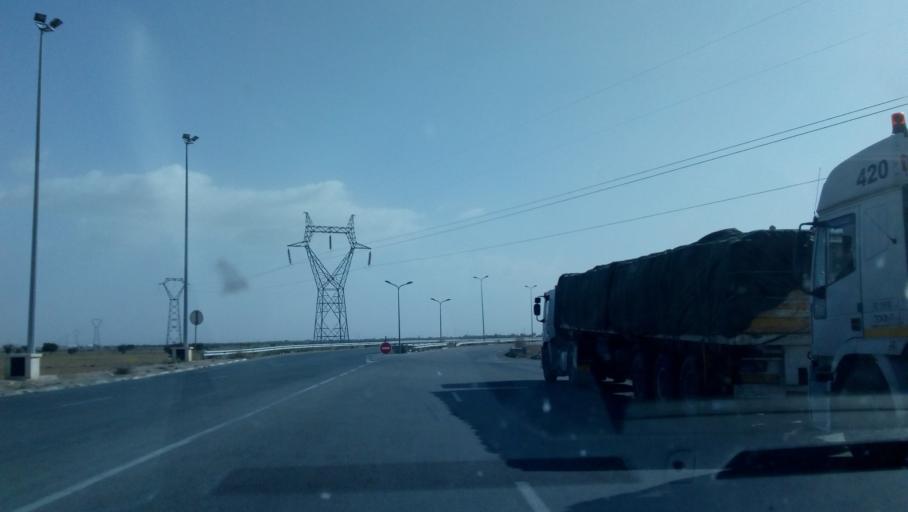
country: TN
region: Qabis
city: Gabes
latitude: 33.8843
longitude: 10.0012
